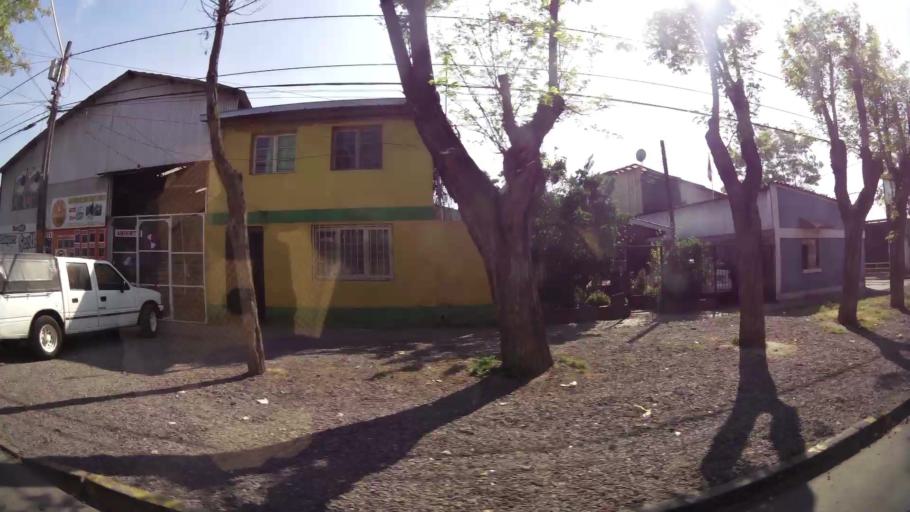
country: CL
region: Santiago Metropolitan
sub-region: Provincia de Santiago
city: Lo Prado
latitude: -33.4260
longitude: -70.7260
